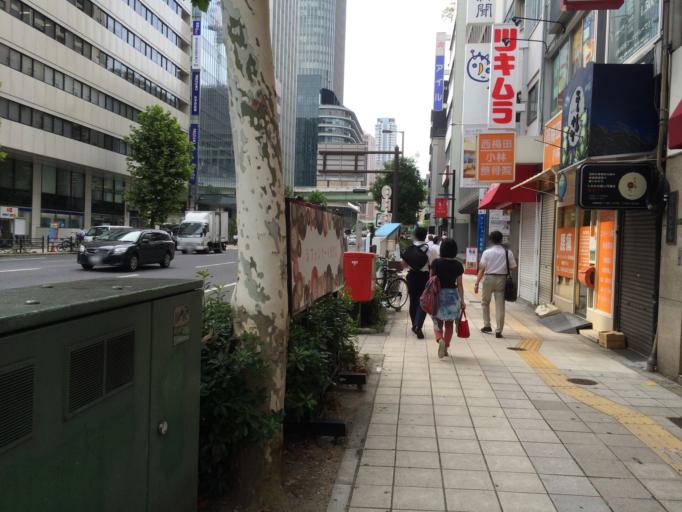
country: JP
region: Osaka
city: Osaka-shi
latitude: 34.6964
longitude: 135.4956
